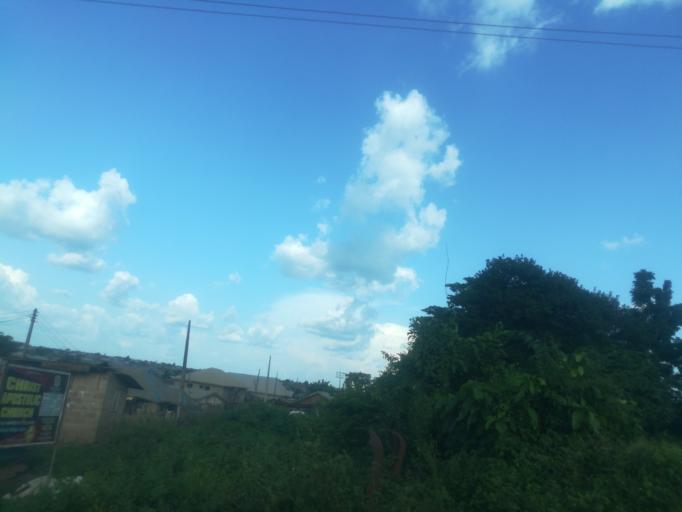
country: NG
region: Oyo
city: Egbeda
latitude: 7.4354
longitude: 3.9823
